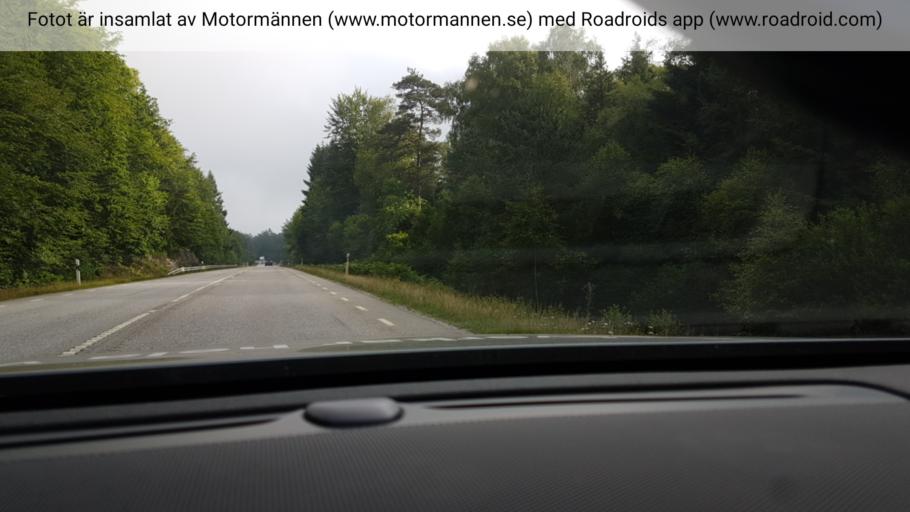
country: SE
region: Skane
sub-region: Hassleholms Kommun
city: Bjarnum
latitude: 56.2611
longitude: 13.7181
